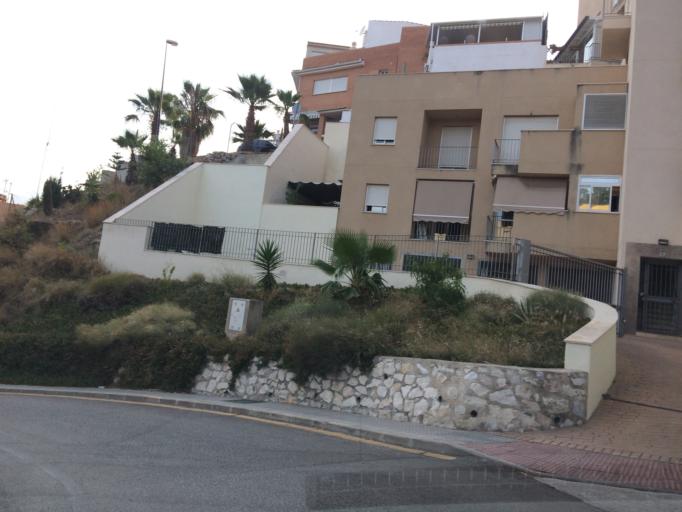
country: ES
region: Andalusia
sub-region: Provincia de Malaga
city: Malaga
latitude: 36.7375
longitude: -4.4139
